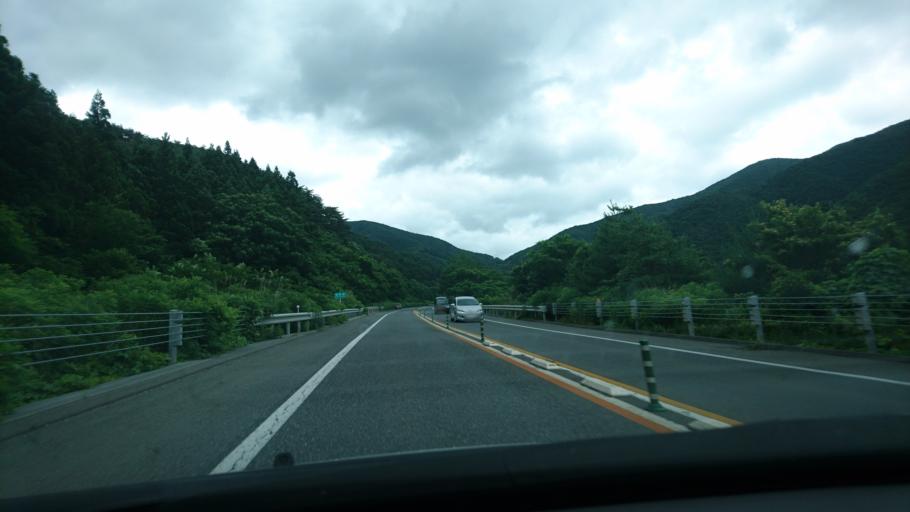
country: JP
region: Iwate
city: Ofunato
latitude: 39.1259
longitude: 141.7526
